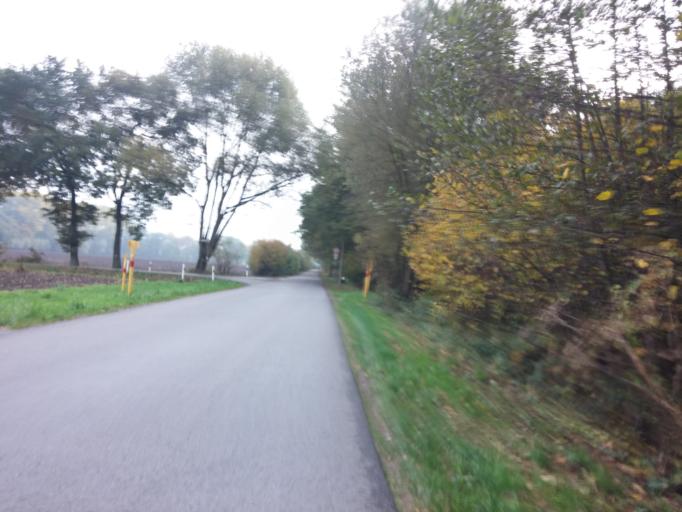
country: DE
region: North Rhine-Westphalia
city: Dorsten
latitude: 51.6365
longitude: 6.9795
